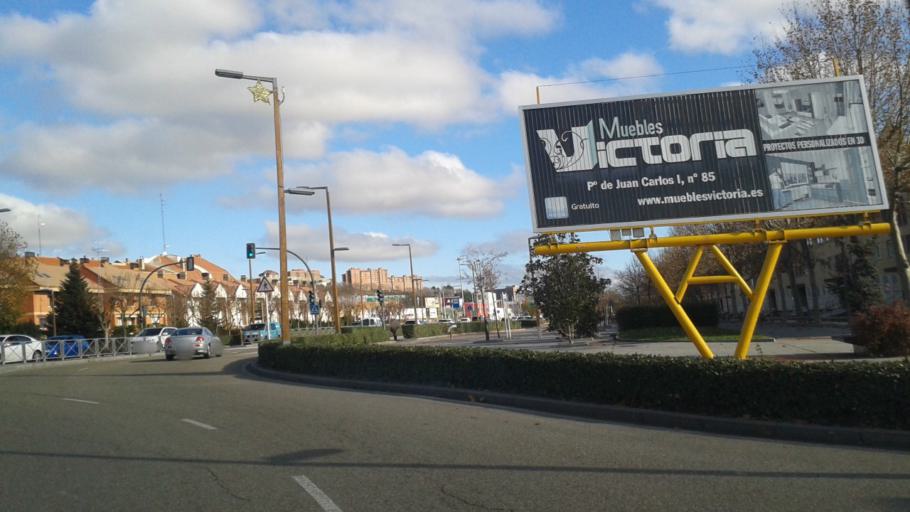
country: ES
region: Castille and Leon
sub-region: Provincia de Valladolid
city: Arroyo
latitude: 41.6241
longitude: -4.7685
